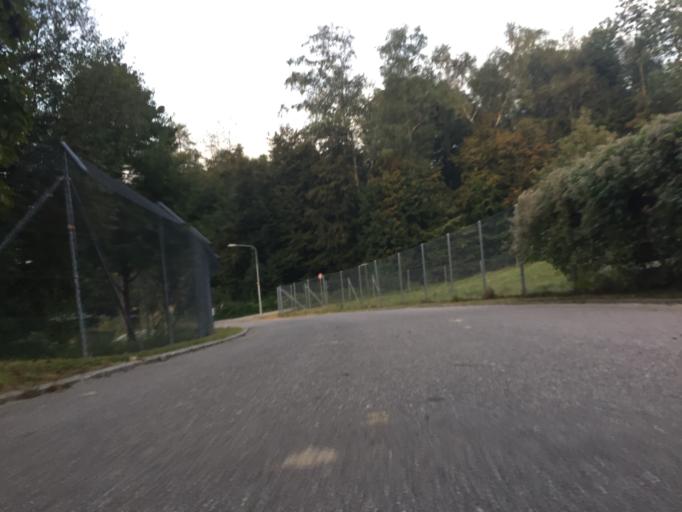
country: CH
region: Zurich
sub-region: Bezirk Zuerich
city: Zuerich (Kreis 7)
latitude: 47.3855
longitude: 8.5784
